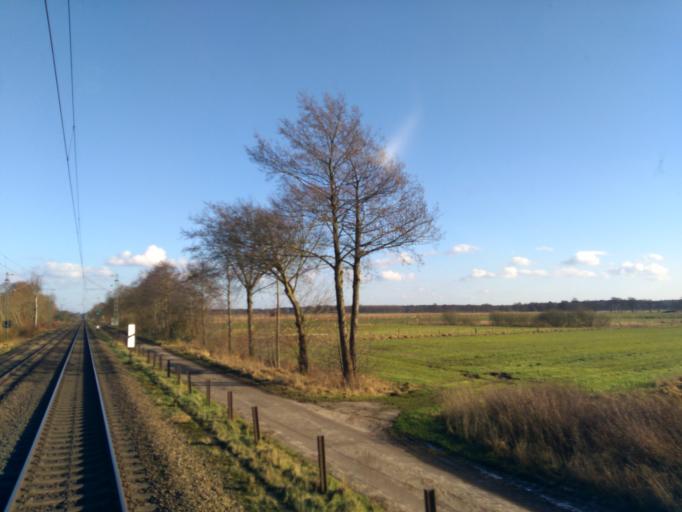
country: DE
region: Lower Saxony
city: Hassendorf
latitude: 53.1018
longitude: 9.2740
